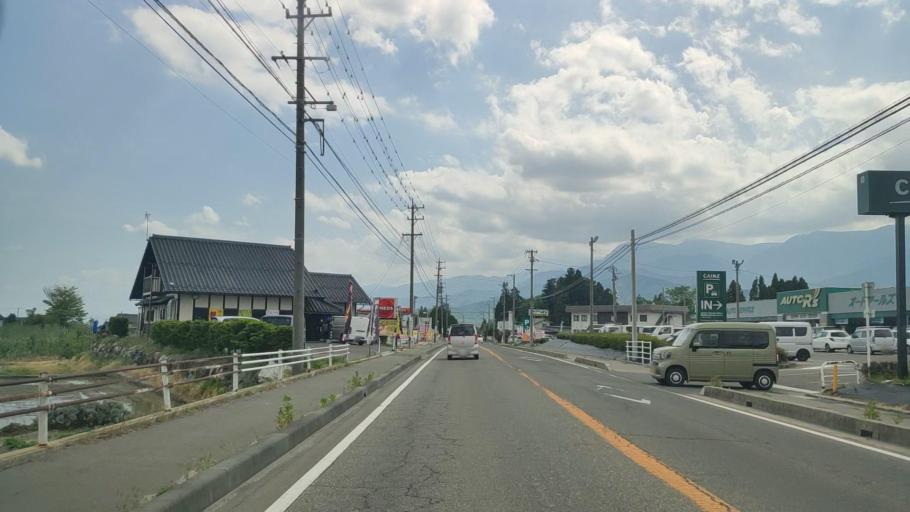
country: JP
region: Nagano
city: Omachi
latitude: 36.4778
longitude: 137.8495
